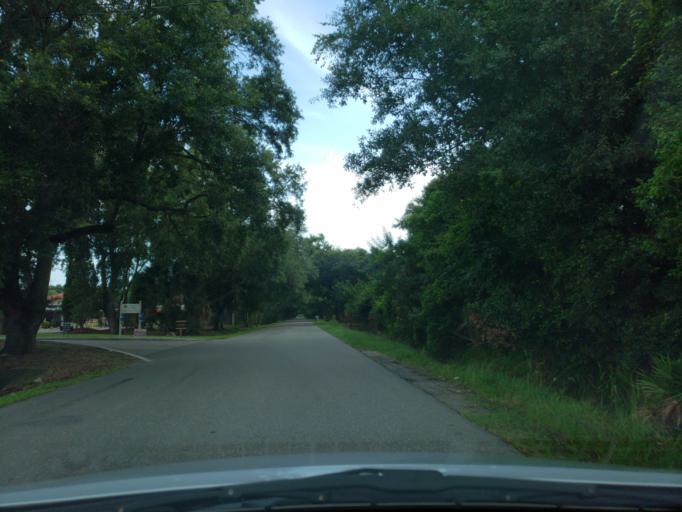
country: US
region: Florida
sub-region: Hillsborough County
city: Palm River-Clair Mel
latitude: 27.9241
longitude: -82.3606
